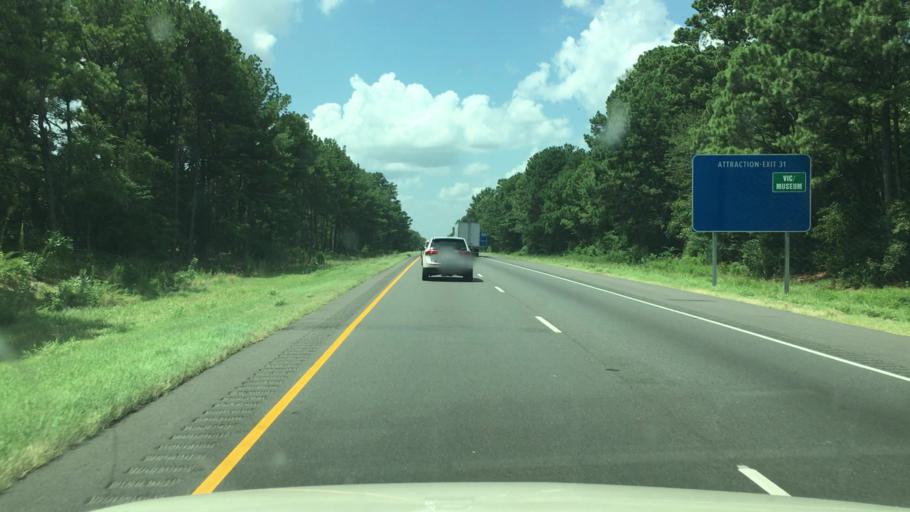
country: US
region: Arkansas
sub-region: Hempstead County
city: Hope
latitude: 33.7106
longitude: -93.5717
